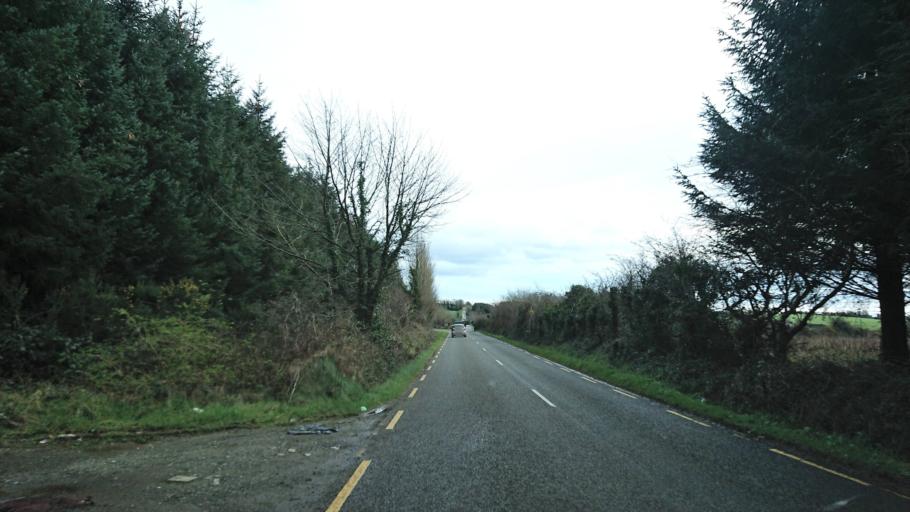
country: IE
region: Munster
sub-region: Waterford
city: Dunmore East
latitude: 52.2420
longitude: -6.8930
